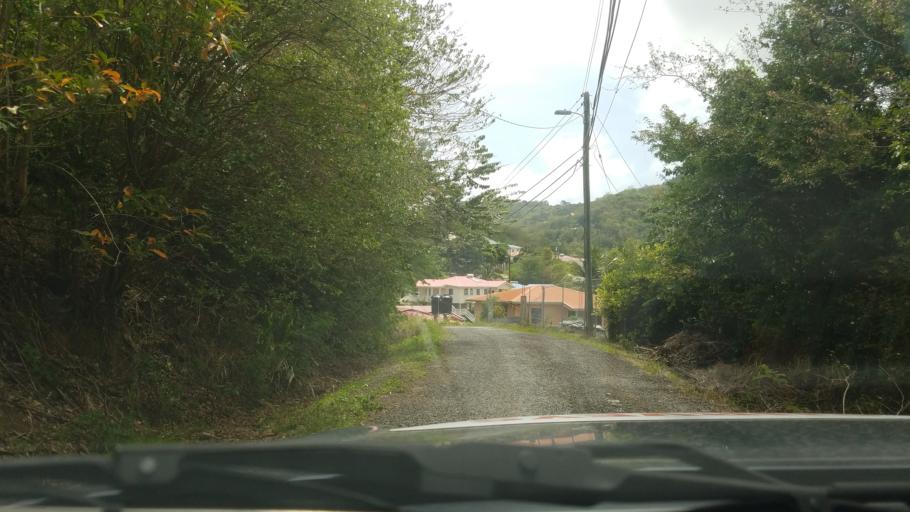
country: LC
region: Gros-Islet
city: Gros Islet
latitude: 14.0461
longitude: -60.9578
